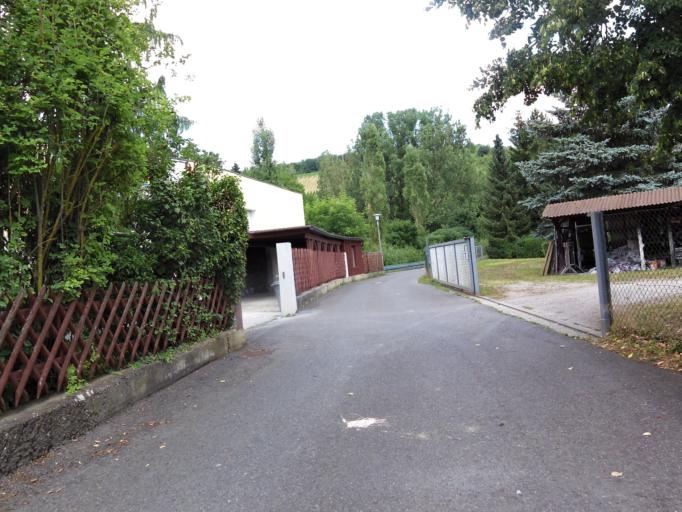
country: DE
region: Bavaria
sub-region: Regierungsbezirk Unterfranken
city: Gerbrunn
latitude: 49.7772
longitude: 9.9962
